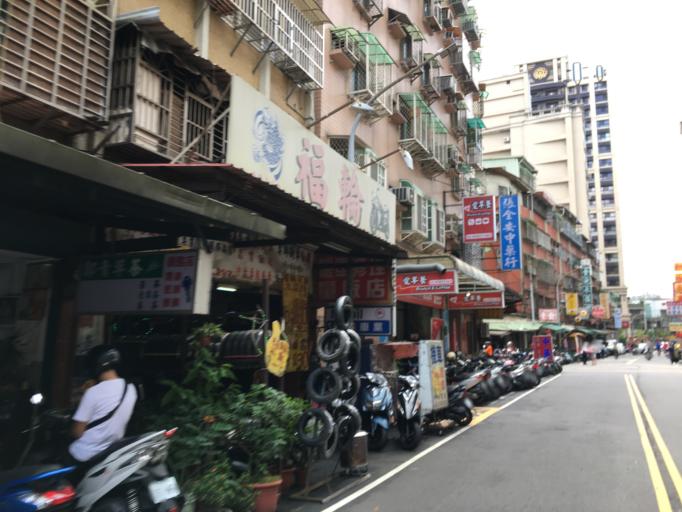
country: TW
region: Taipei
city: Taipei
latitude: 25.0808
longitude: 121.4909
